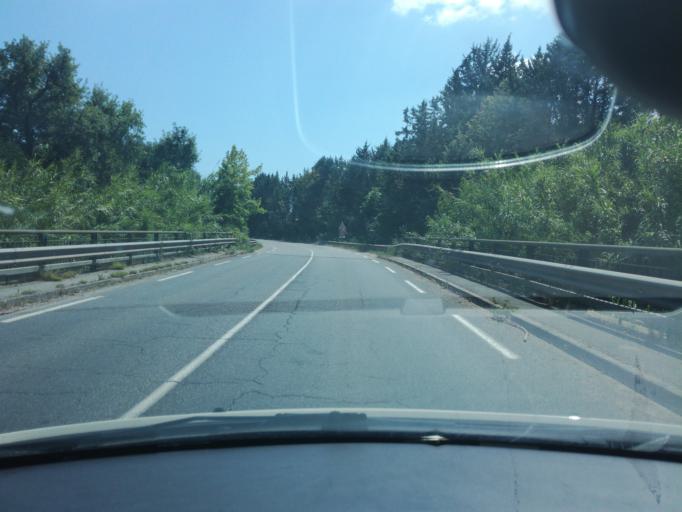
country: FR
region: Provence-Alpes-Cote d'Azur
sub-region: Departement du Var
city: Le Muy
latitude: 43.4814
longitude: 6.5655
